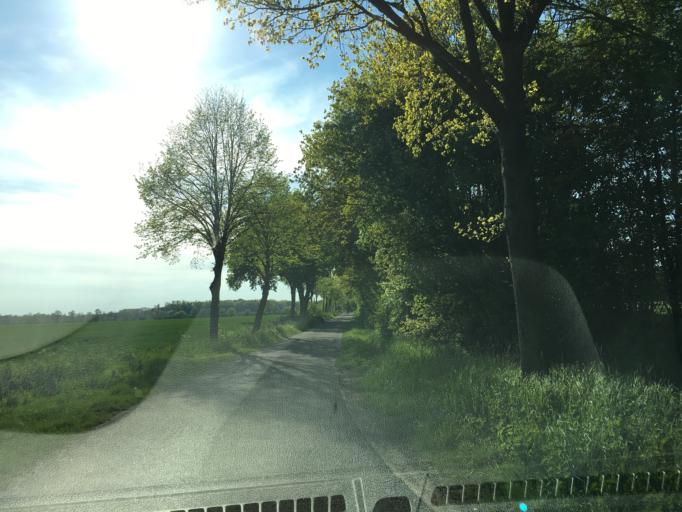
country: DE
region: North Rhine-Westphalia
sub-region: Regierungsbezirk Munster
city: Nordkirchen
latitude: 51.7524
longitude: 7.5202
